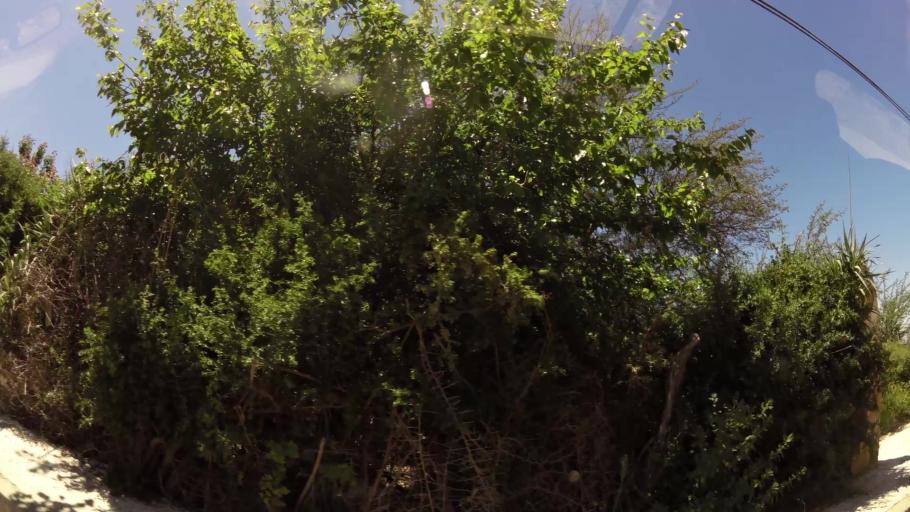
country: MA
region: Meknes-Tafilalet
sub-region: Meknes
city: Meknes
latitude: 33.9028
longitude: -5.5638
